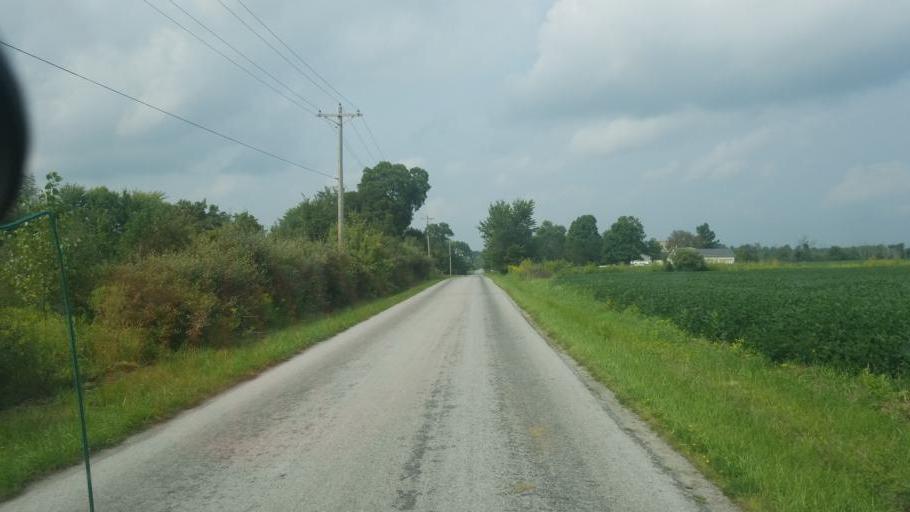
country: US
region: Ohio
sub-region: Wayne County
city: West Salem
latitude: 41.0457
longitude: -82.2017
